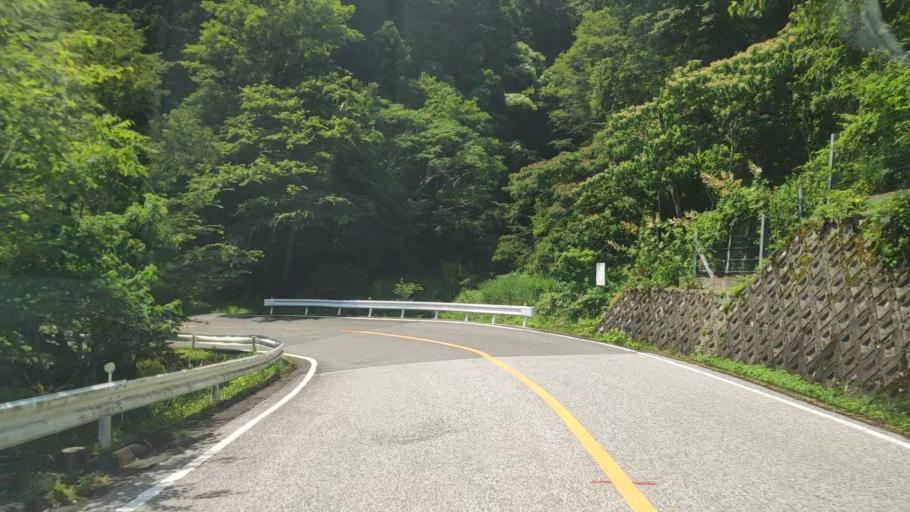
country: JP
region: Gifu
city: Tarui
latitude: 35.3809
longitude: 136.4447
